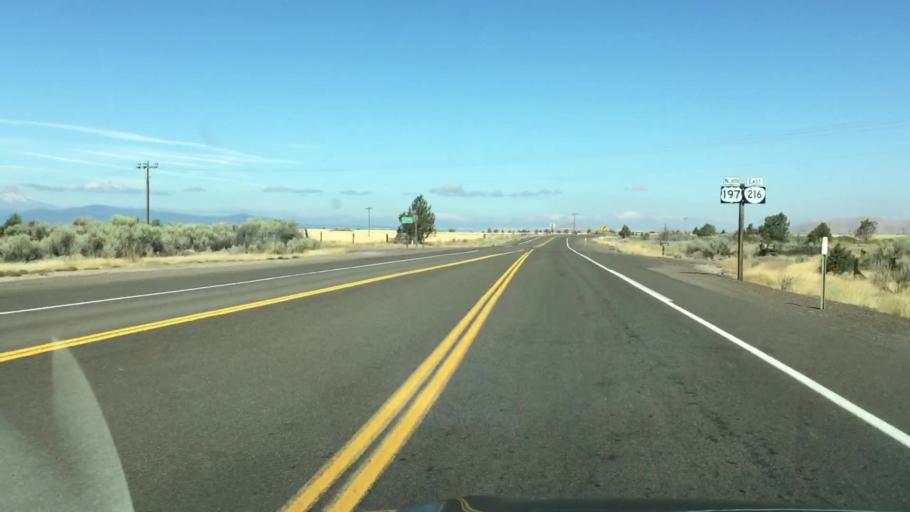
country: US
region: Oregon
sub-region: Wasco County
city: The Dalles
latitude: 45.1712
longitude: -121.1213
